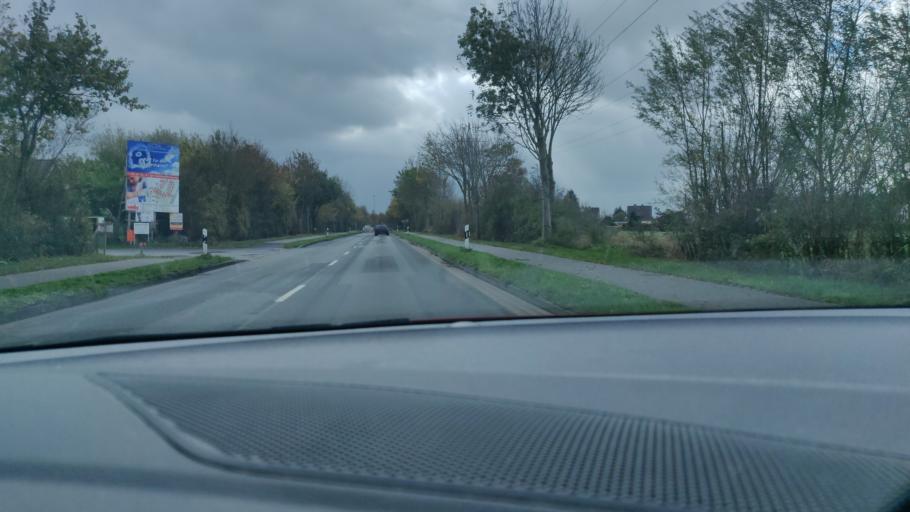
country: DE
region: Lower Saxony
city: Cuxhaven
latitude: 53.8515
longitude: 8.6731
